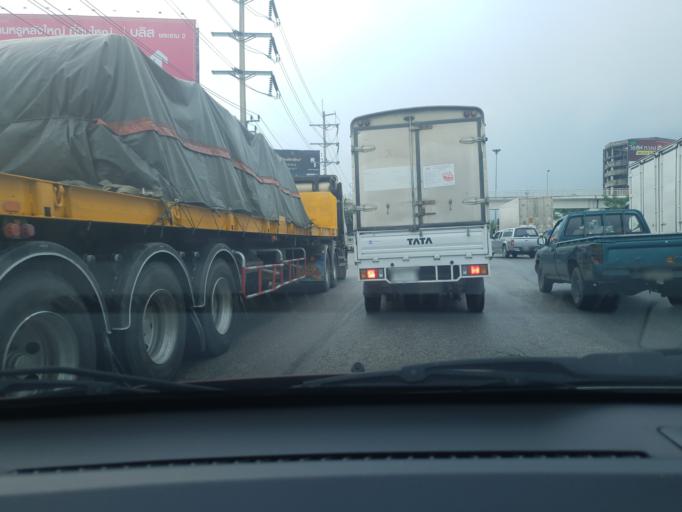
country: TH
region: Bangkok
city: Bang Bon
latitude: 13.6392
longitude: 100.4069
